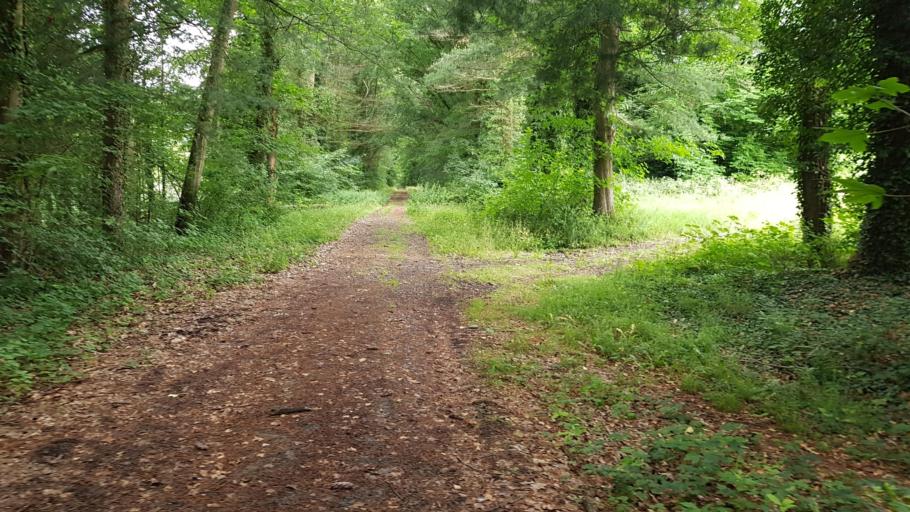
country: BE
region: Wallonia
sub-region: Province de Namur
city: Dinant
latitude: 50.2201
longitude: 4.9195
